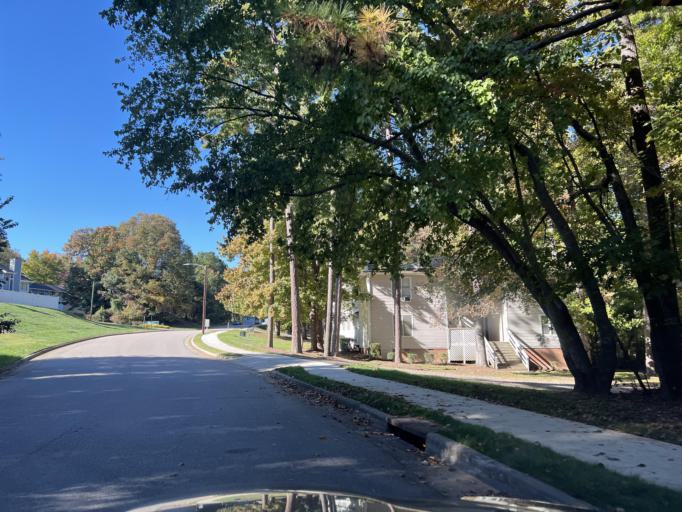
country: US
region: North Carolina
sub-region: Wake County
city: West Raleigh
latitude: 35.8882
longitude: -78.6426
